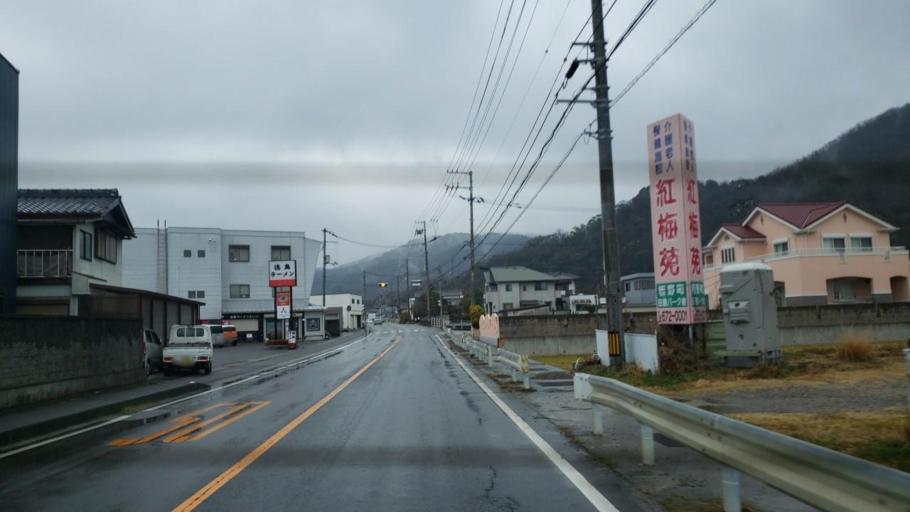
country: JP
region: Tokushima
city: Narutocho-mitsuishi
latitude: 34.1613
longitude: 134.5486
